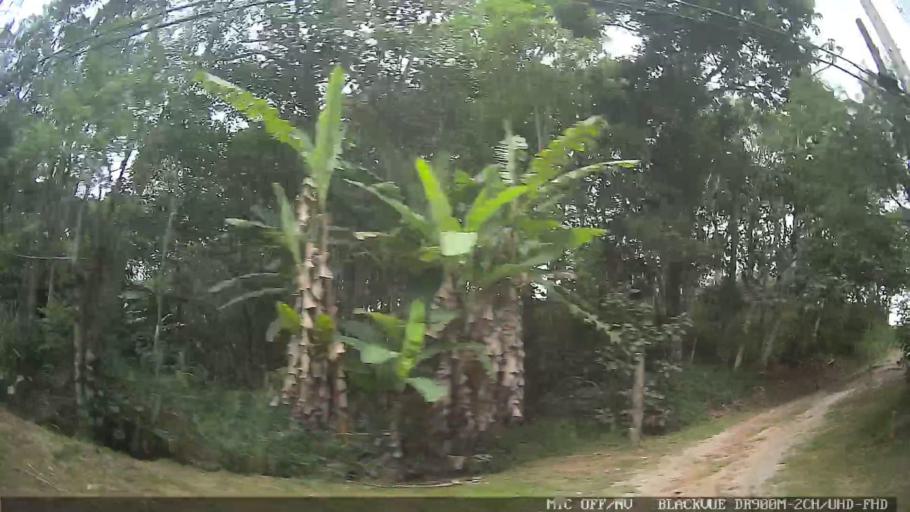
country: BR
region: Sao Paulo
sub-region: Biritiba-Mirim
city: Biritiba Mirim
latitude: -23.5433
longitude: -46.0871
